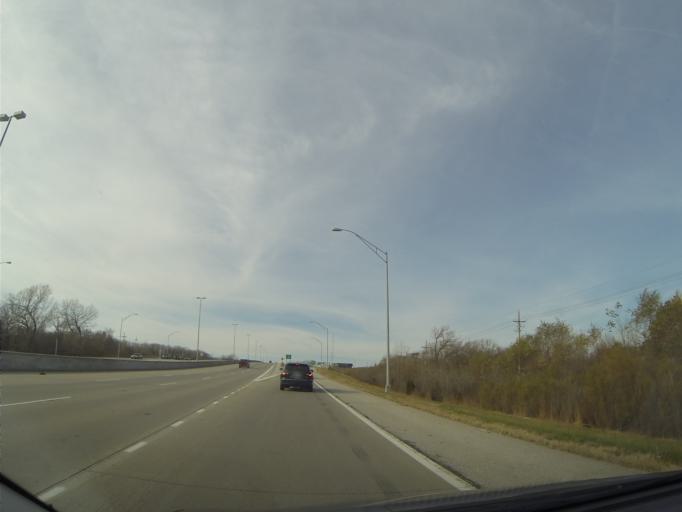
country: US
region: Nebraska
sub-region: Douglas County
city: Elkhorn
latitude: 41.2630
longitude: -96.2293
